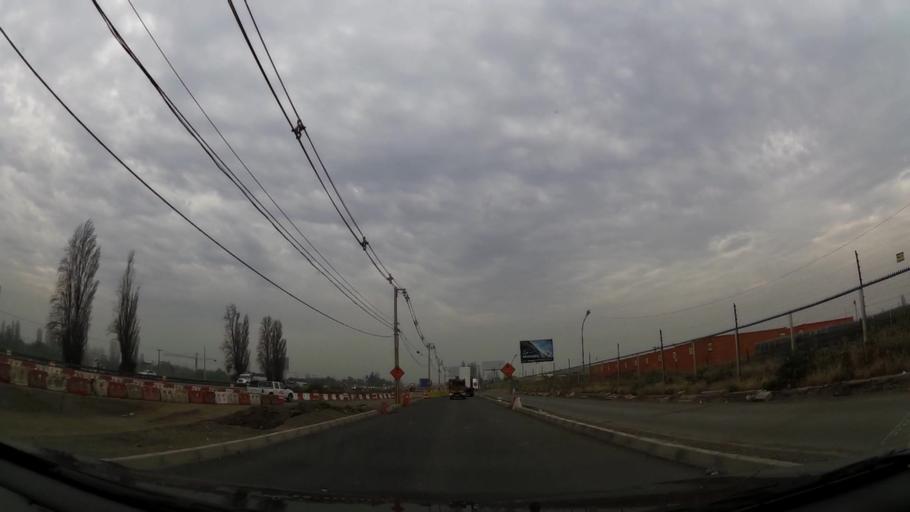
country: CL
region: Santiago Metropolitan
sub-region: Provincia de Chacabuco
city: Chicureo Abajo
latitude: -33.2655
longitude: -70.7460
